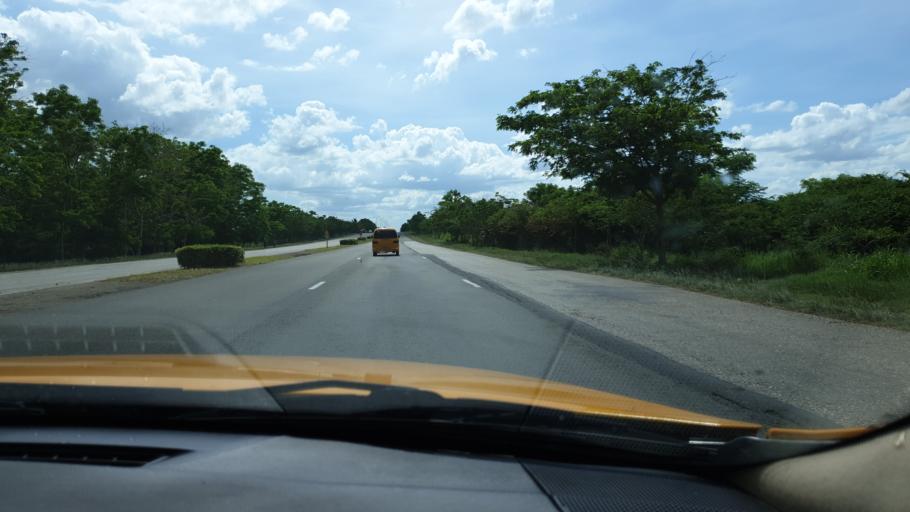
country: CU
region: Cienfuegos
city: Cruces
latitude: 22.4524
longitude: -80.2867
